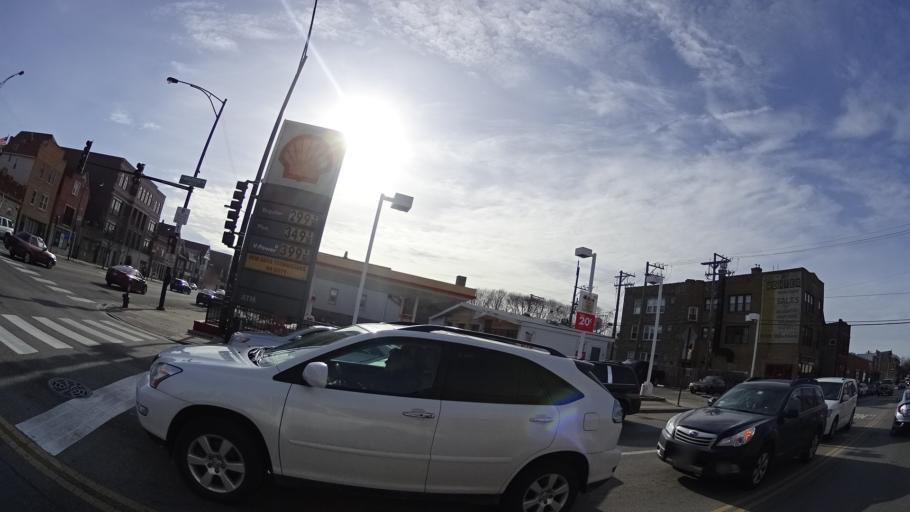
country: US
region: Illinois
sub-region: Cook County
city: Lincolnwood
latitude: 41.9614
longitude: -87.6889
